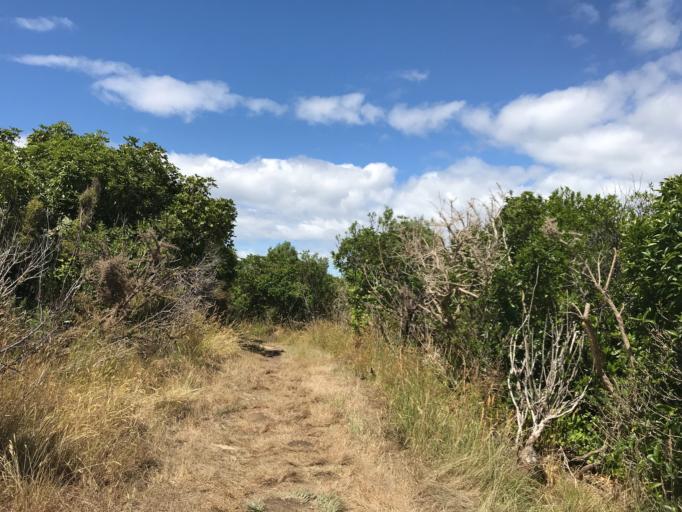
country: NZ
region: Marlborough
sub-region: Marlborough District
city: Picton
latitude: -41.2077
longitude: 174.0226
